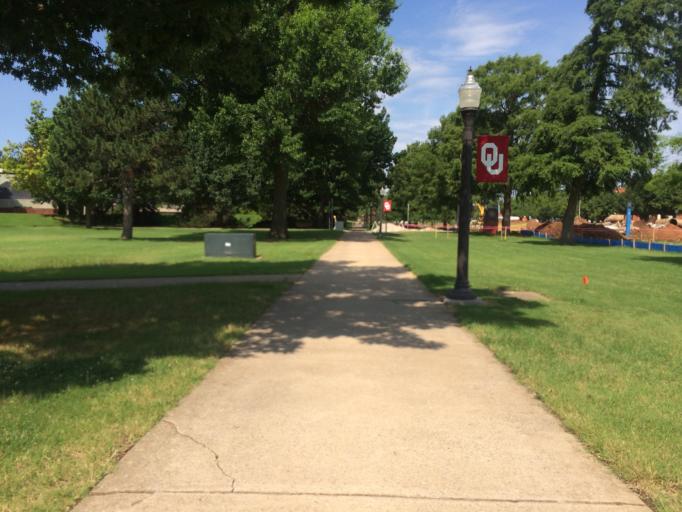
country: US
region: Oklahoma
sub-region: Cleveland County
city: Norman
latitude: 35.1964
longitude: -97.4436
